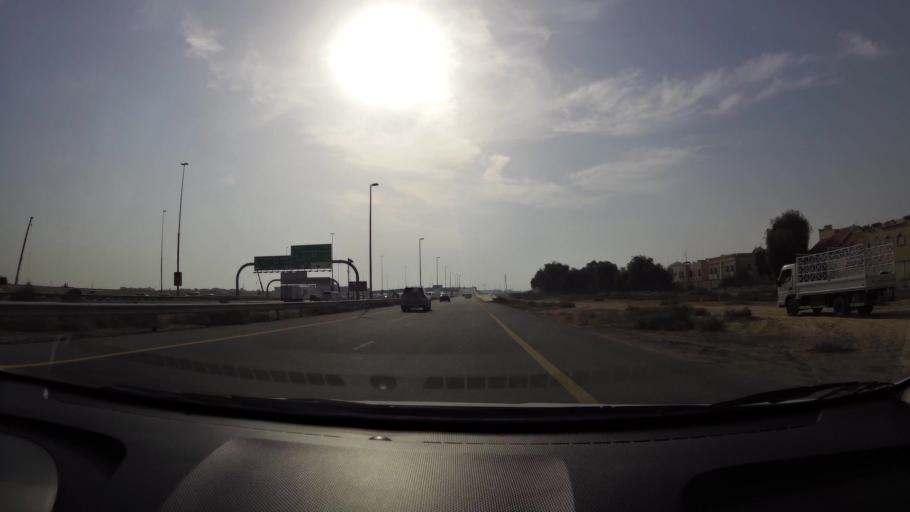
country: AE
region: Ash Shariqah
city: Sharjah
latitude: 25.2353
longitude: 55.4143
